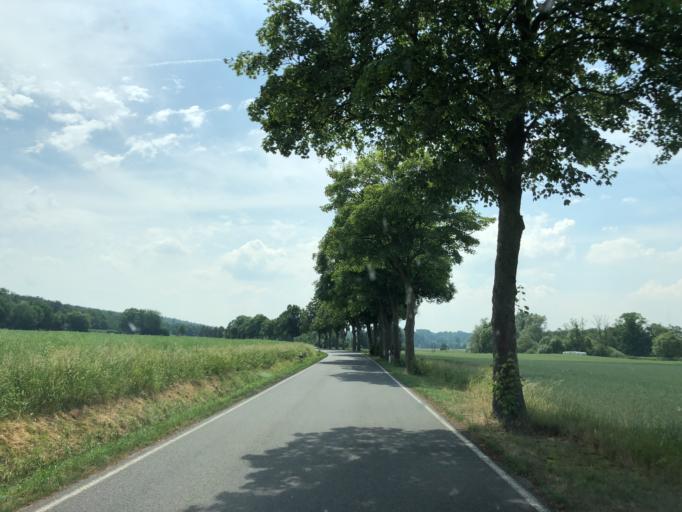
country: DE
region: Hesse
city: Schwalmstadt
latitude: 50.9423
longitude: 9.2019
